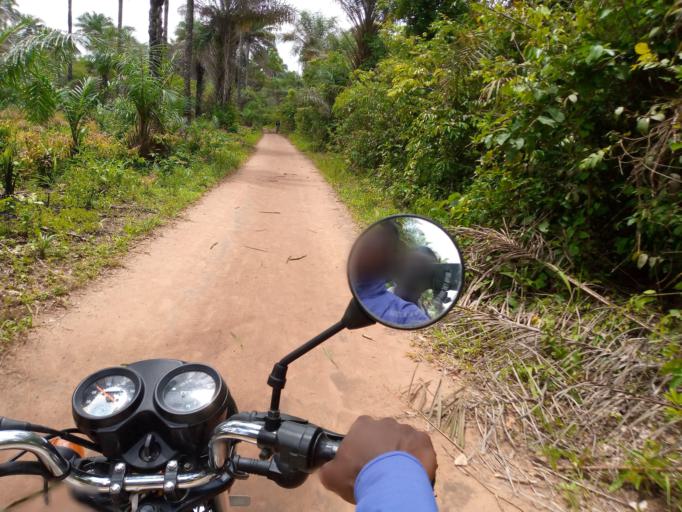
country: SL
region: Northern Province
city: Mange
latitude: 8.9740
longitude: -12.8240
